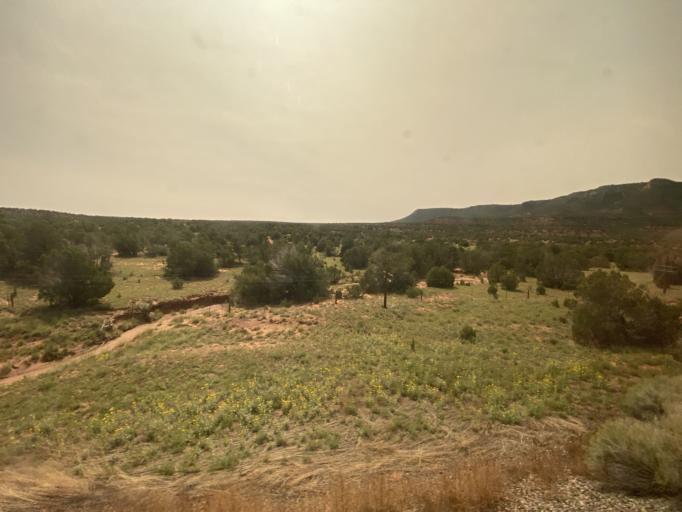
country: US
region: New Mexico
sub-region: San Miguel County
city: Pecos
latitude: 35.3941
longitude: -105.4862
